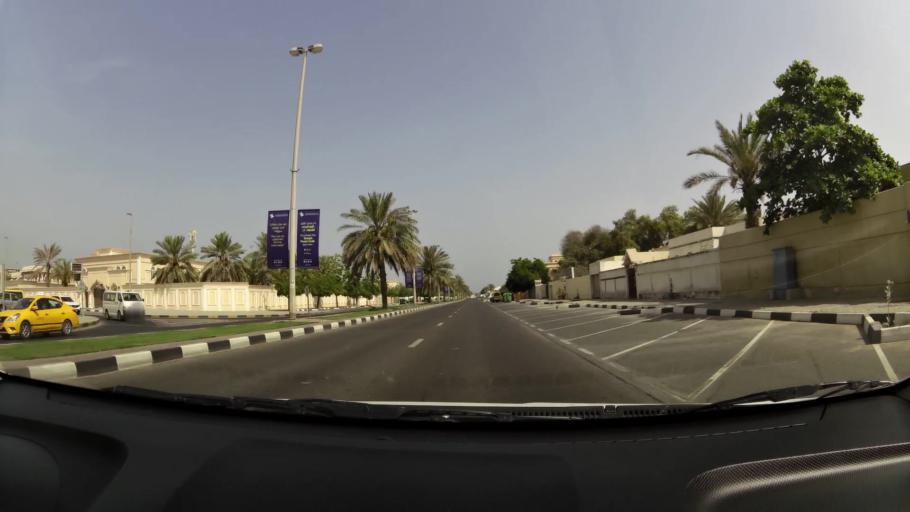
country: AE
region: Ash Shariqah
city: Sharjah
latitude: 25.3589
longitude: 55.4251
